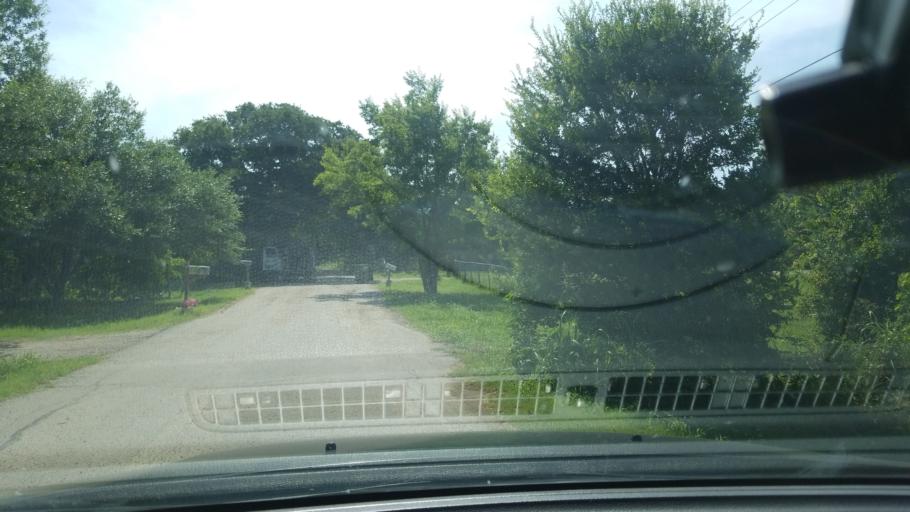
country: US
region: Texas
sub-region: Dallas County
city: Balch Springs
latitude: 32.7278
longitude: -96.6294
